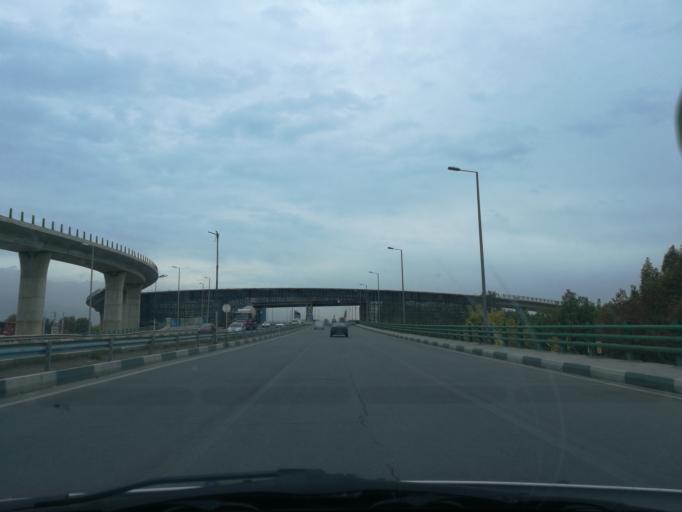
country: IR
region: Alborz
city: Karaj
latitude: 35.8510
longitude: 50.9059
